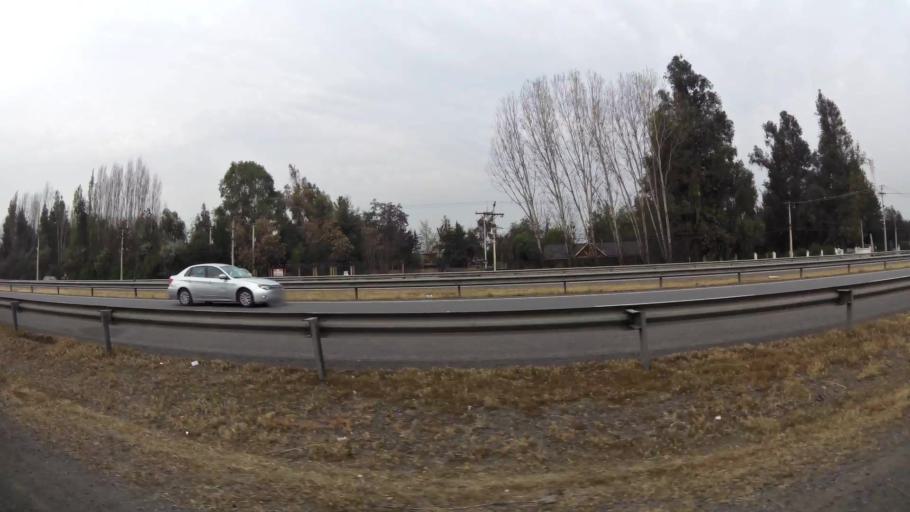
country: CL
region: Santiago Metropolitan
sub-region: Provincia de Chacabuco
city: Chicureo Abajo
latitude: -33.2685
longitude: -70.7002
